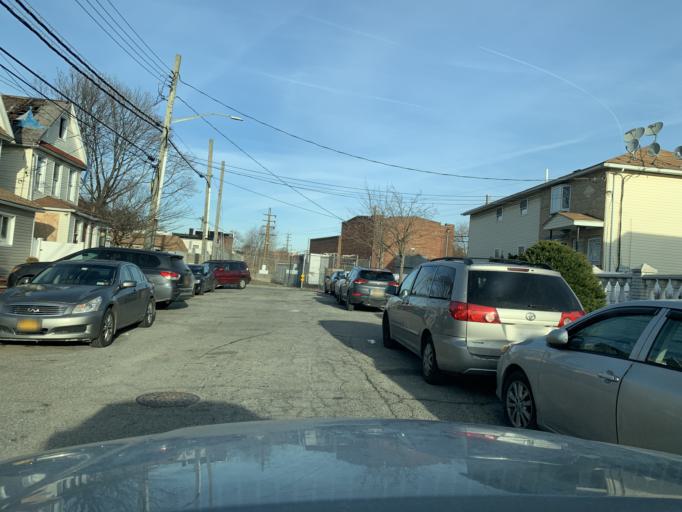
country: US
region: New York
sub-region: Queens County
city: Jamaica
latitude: 40.6911
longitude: -73.7920
